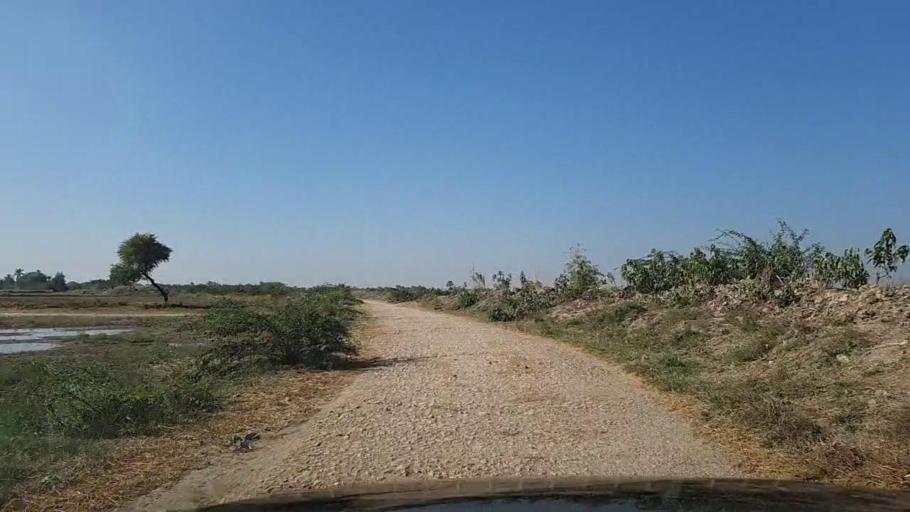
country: PK
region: Sindh
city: Thatta
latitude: 24.7159
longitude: 67.9205
